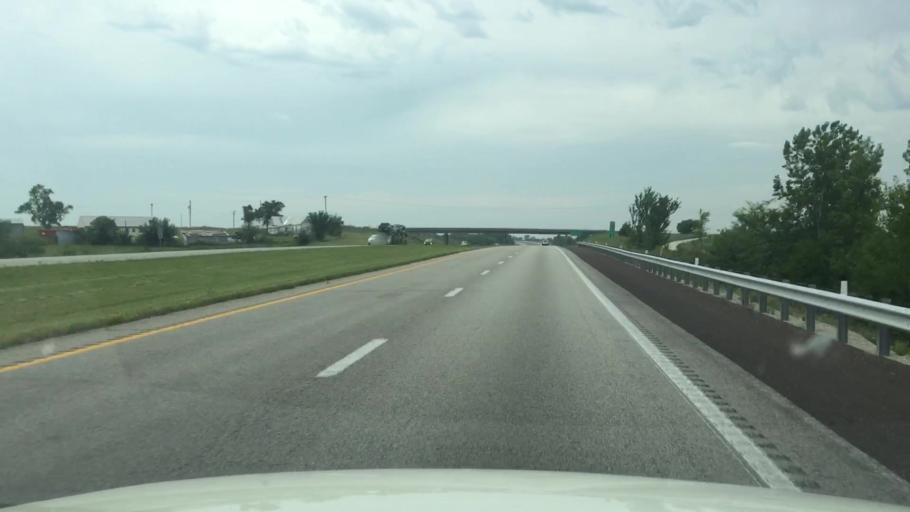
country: US
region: Missouri
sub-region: Daviess County
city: Gallatin
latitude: 39.9341
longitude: -94.1285
